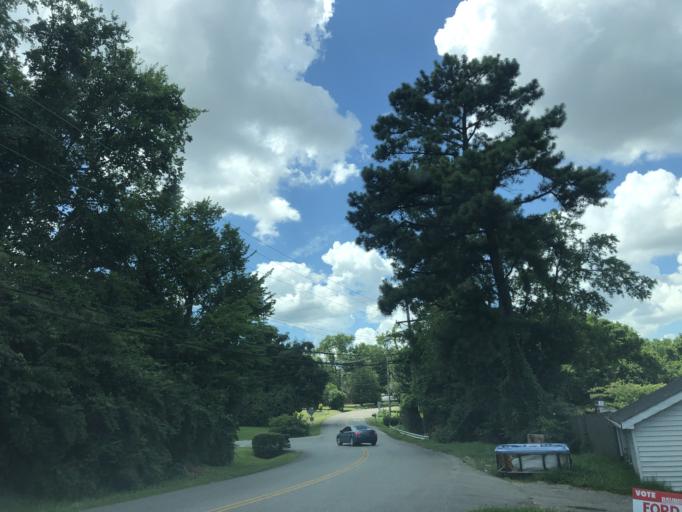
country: US
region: Tennessee
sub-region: Davidson County
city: Oak Hill
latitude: 36.0752
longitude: -86.7168
